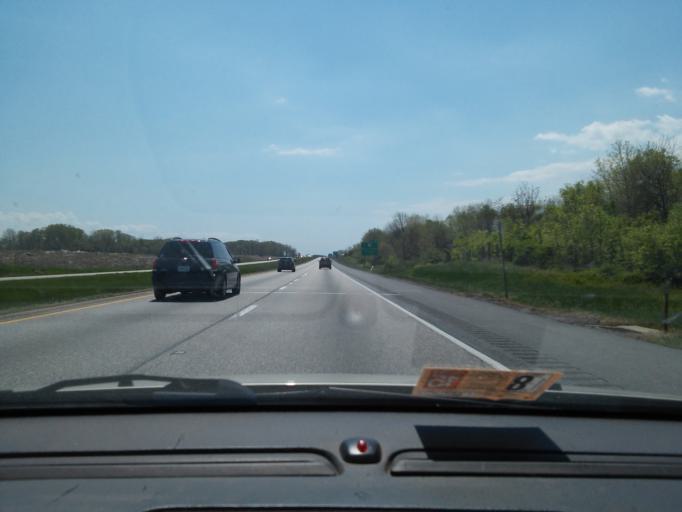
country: US
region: Pennsylvania
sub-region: Franklin County
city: Greencastle
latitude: 39.7736
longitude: -77.7188
